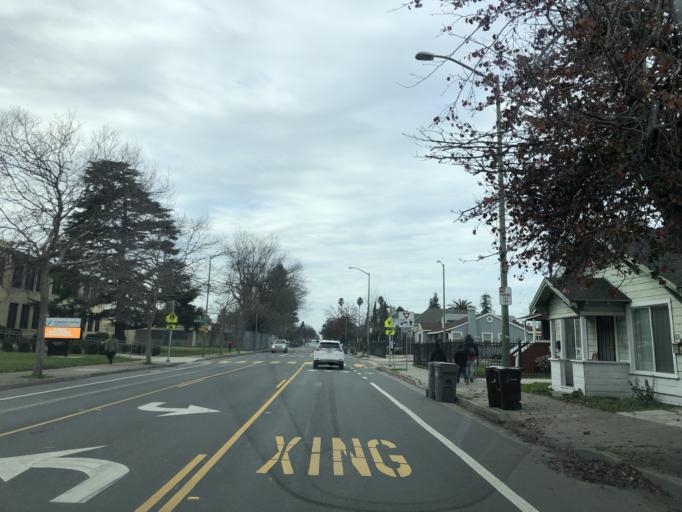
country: US
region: California
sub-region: Alameda County
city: San Leandro
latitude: 37.7467
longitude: -122.1657
